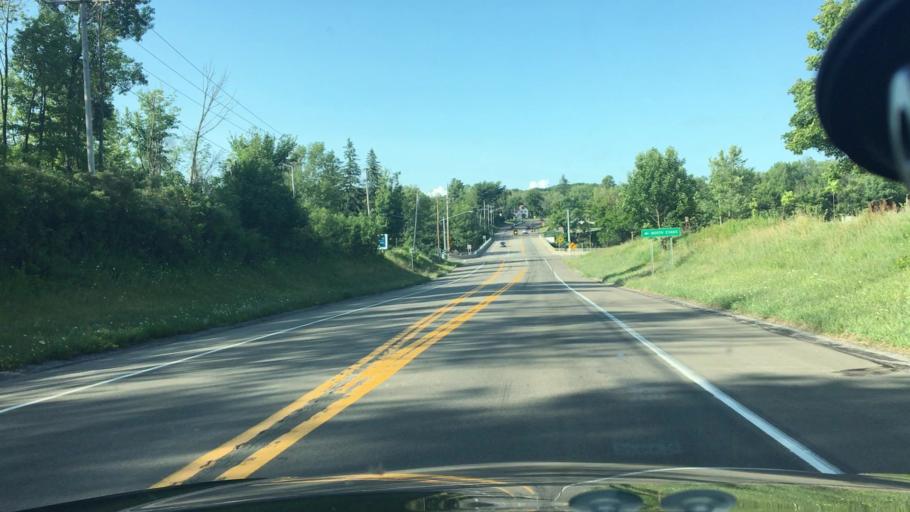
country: US
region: New York
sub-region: Erie County
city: Eden
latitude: 42.6938
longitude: -78.9375
